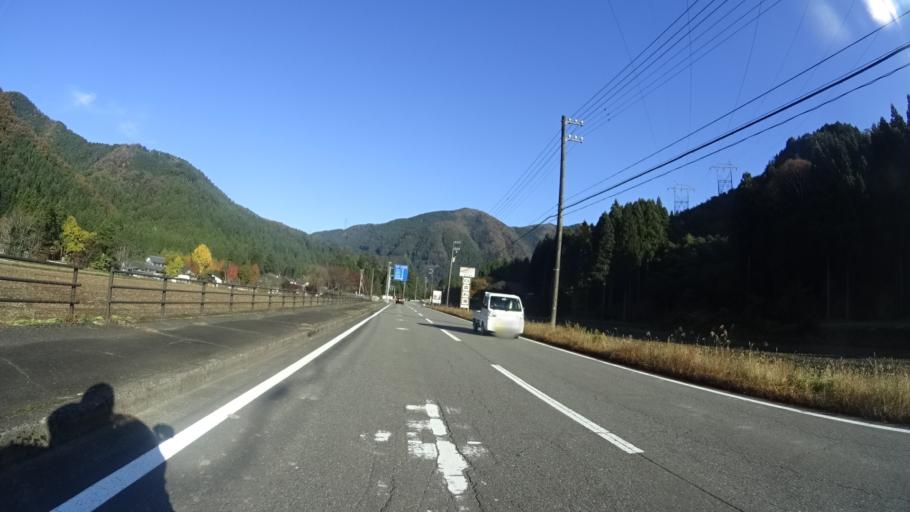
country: JP
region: Fukui
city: Maruoka
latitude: 36.1645
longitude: 136.3323
